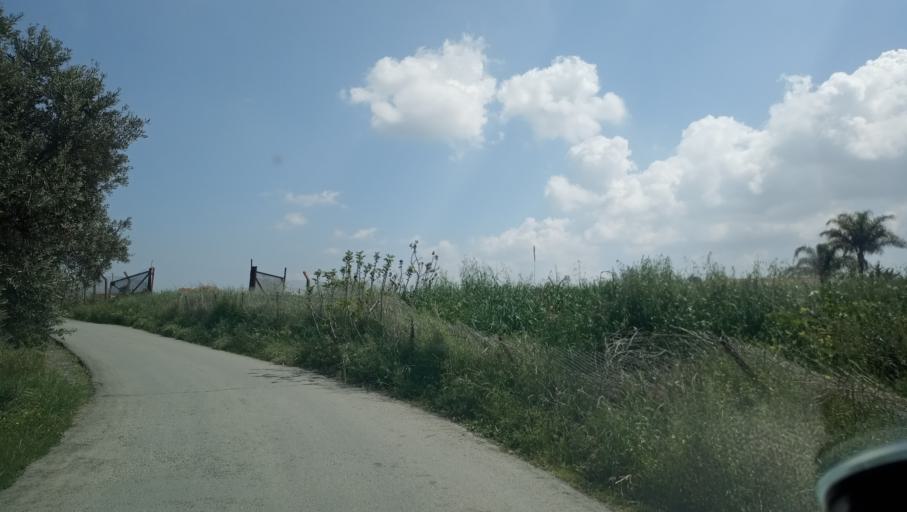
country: CY
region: Lefkosia
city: Dali
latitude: 35.0197
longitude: 33.4046
